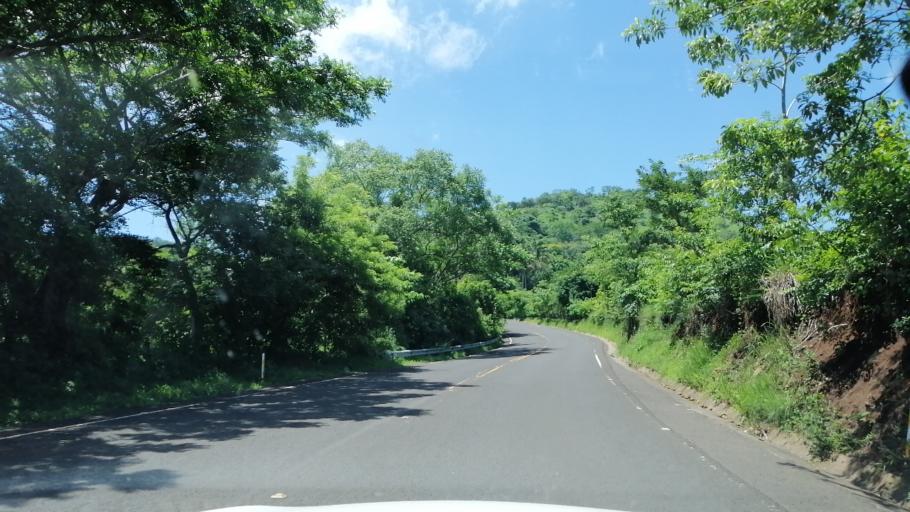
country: SV
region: San Miguel
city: Ciudad Barrios
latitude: 13.8024
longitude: -88.2991
